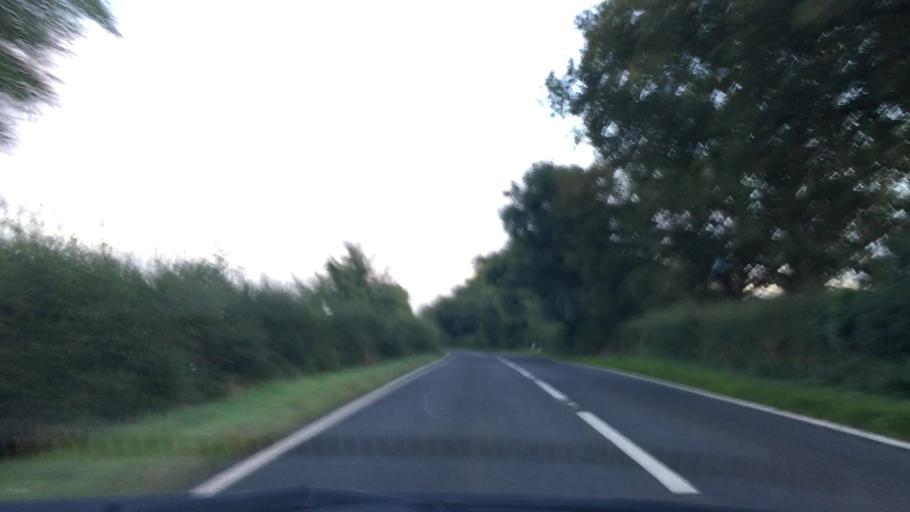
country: GB
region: England
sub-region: North East Lincolnshire
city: Wold Newton
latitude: 53.4639
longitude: -0.0999
